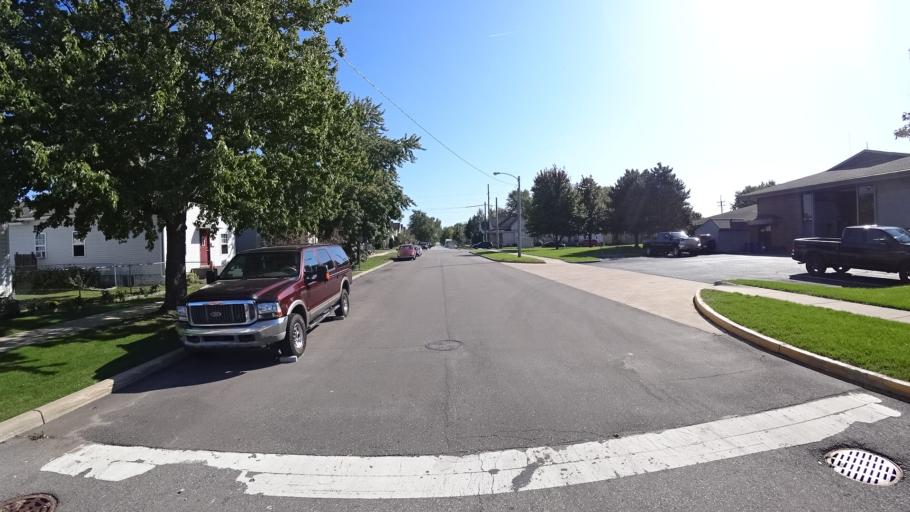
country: US
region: Indiana
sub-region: LaPorte County
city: Michigan City
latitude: 41.7103
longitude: -86.9054
